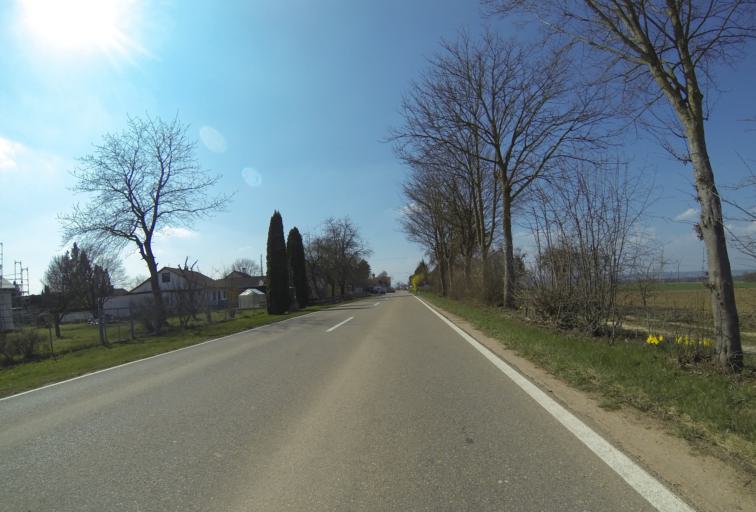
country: DE
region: Baden-Wuerttemberg
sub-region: Tuebingen Region
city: Huttisheim
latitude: 48.2947
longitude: 9.9489
